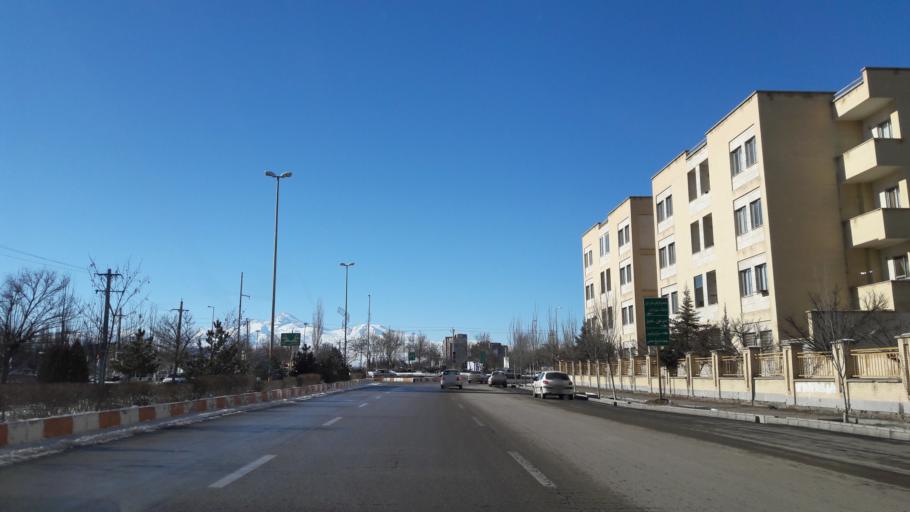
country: IR
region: Ardabil
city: Ardabil
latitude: 38.2187
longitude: 48.2970
